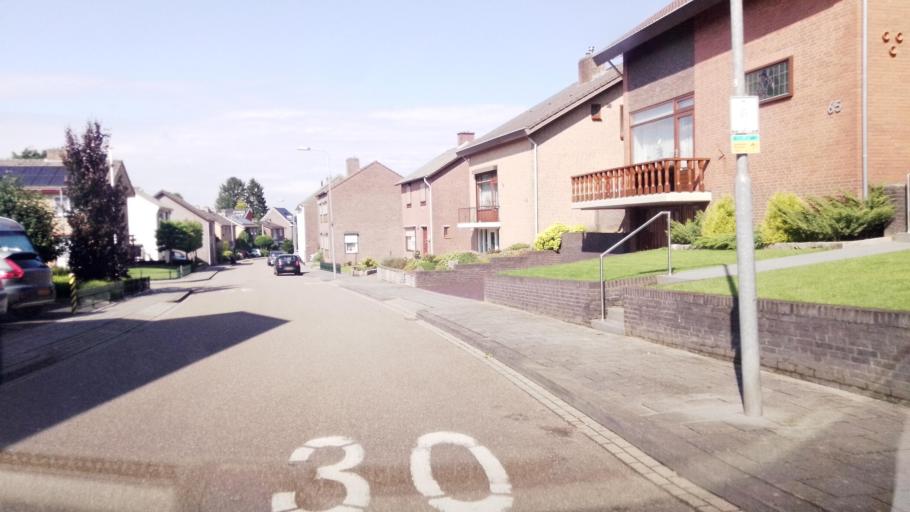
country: NL
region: Limburg
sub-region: Gemeente Voerendaal
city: Klimmen
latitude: 50.8861
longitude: 5.8572
